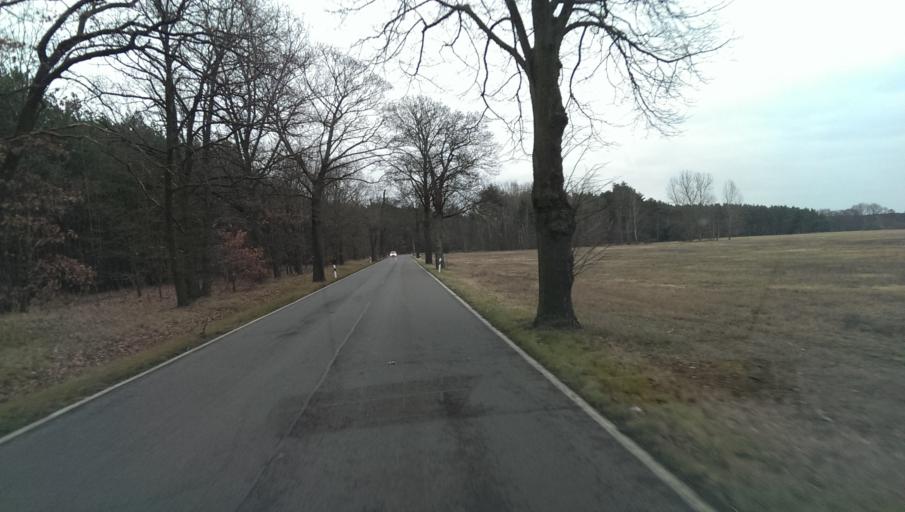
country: DE
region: Brandenburg
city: Mittenwalde
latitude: 52.2225
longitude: 13.5352
